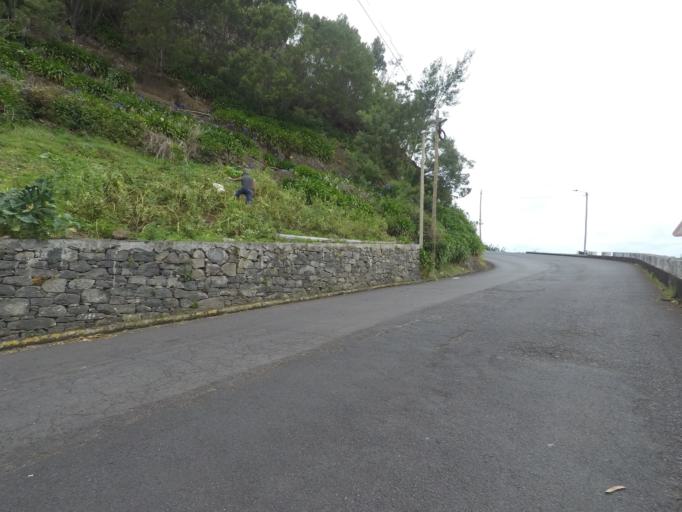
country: PT
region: Madeira
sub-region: Santana
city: Santana
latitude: 32.7942
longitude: -16.8627
